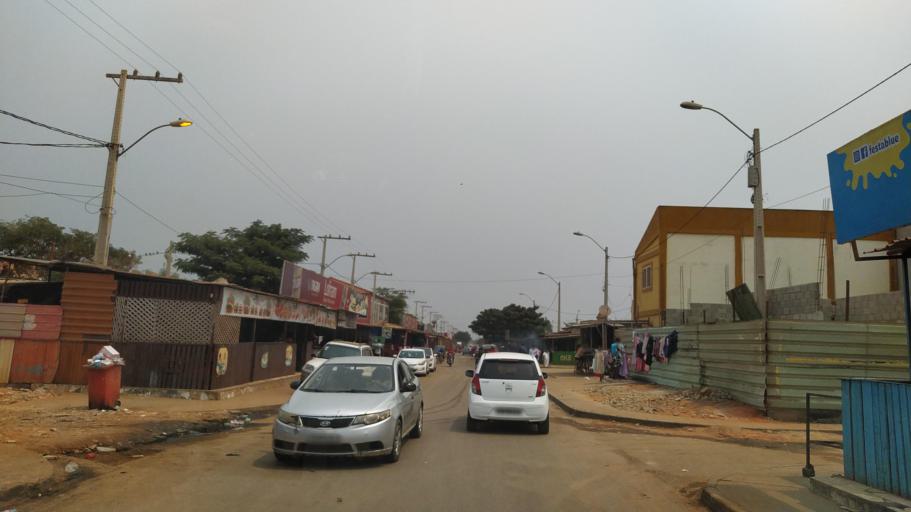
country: AO
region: Luanda
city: Luanda
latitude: -9.0722
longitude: 13.4073
